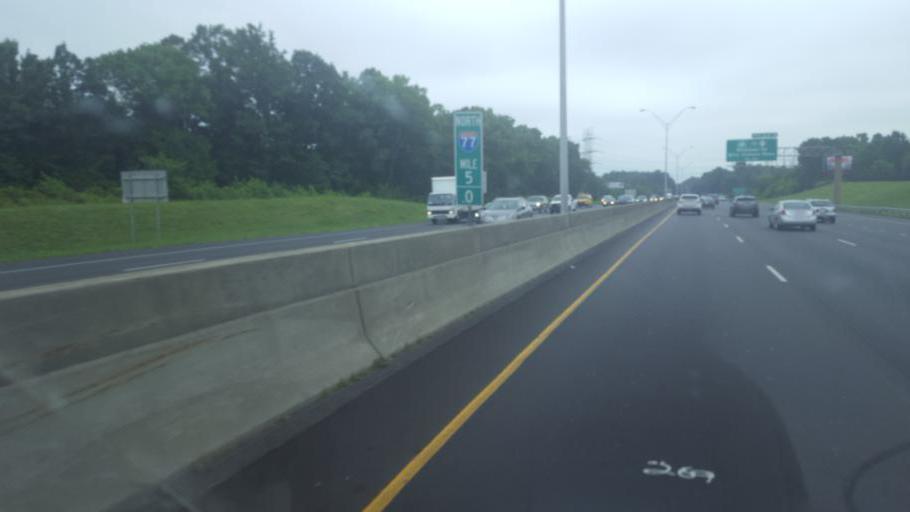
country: US
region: North Carolina
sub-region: Mecklenburg County
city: Charlotte
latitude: 35.1679
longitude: -80.8884
